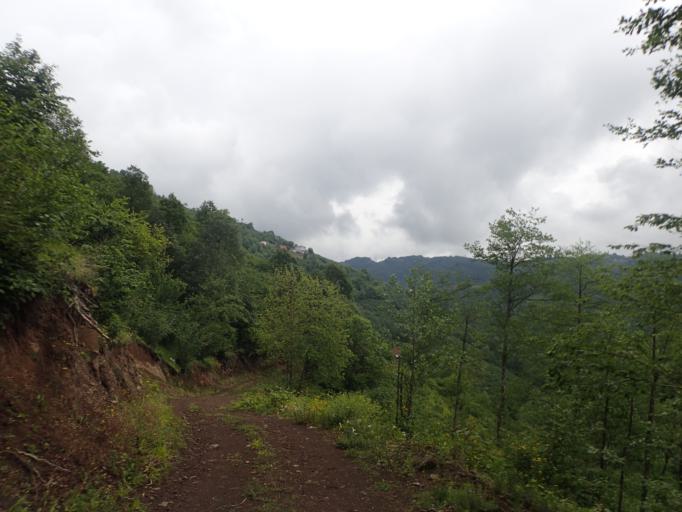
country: TR
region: Samsun
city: Salipazari
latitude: 40.9372
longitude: 36.8931
